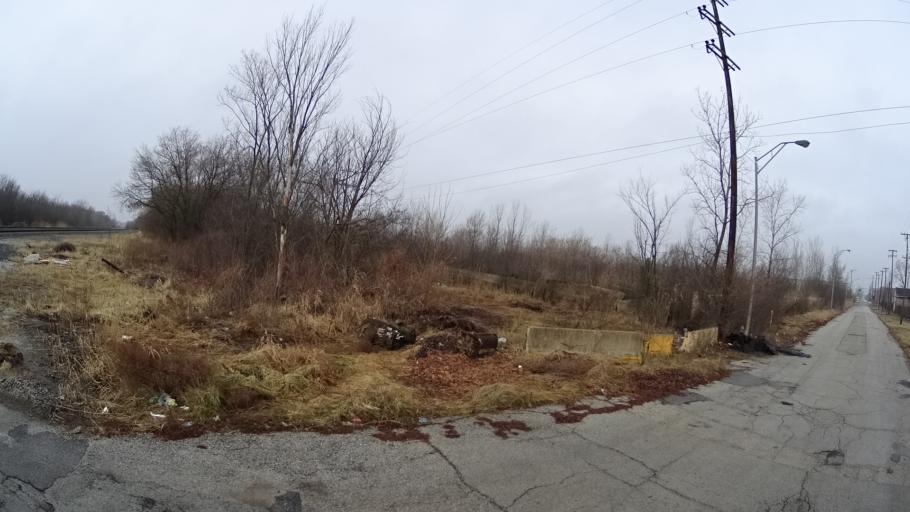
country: US
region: Illinois
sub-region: Cook County
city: Chicago Heights
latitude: 41.4990
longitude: -87.6210
